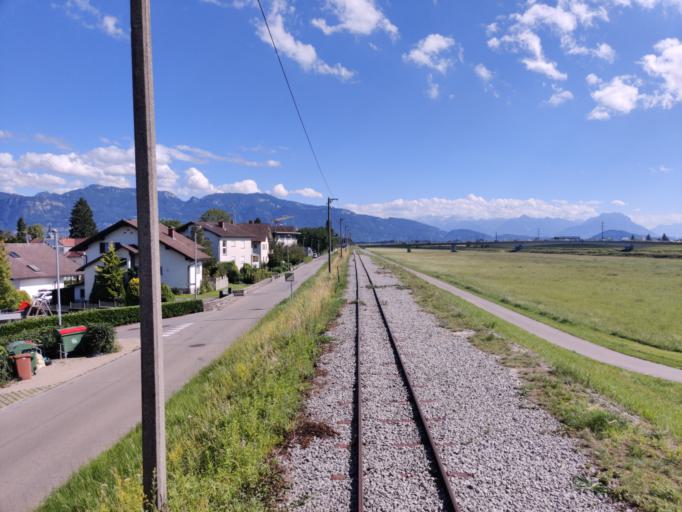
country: CH
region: Saint Gallen
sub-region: Wahlkreis Rheintal
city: Au
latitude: 47.4351
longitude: 9.6464
